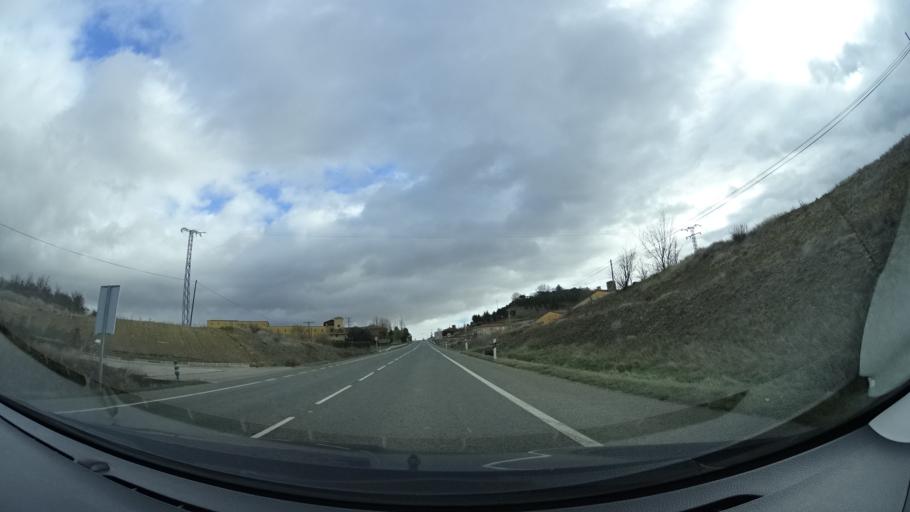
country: ES
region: Basque Country
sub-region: Provincia de Alava
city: Laguardia
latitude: 42.5599
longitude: -2.5902
